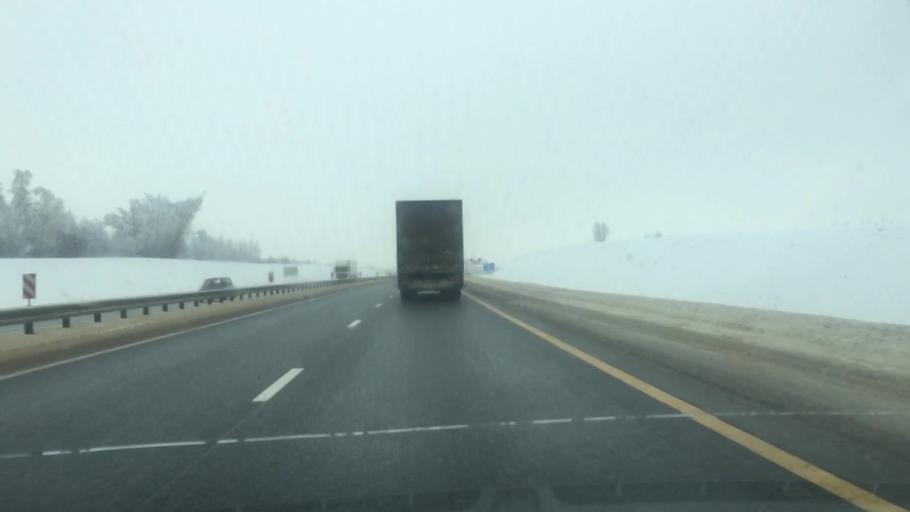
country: RU
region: Lipetsk
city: Yelets
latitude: 52.5628
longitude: 38.7111
